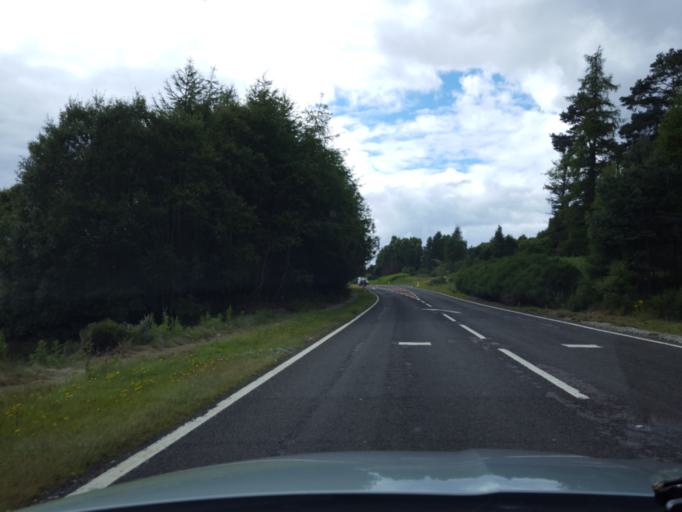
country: GB
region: Scotland
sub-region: Highland
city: Grantown on Spey
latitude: 57.2921
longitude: -3.6656
